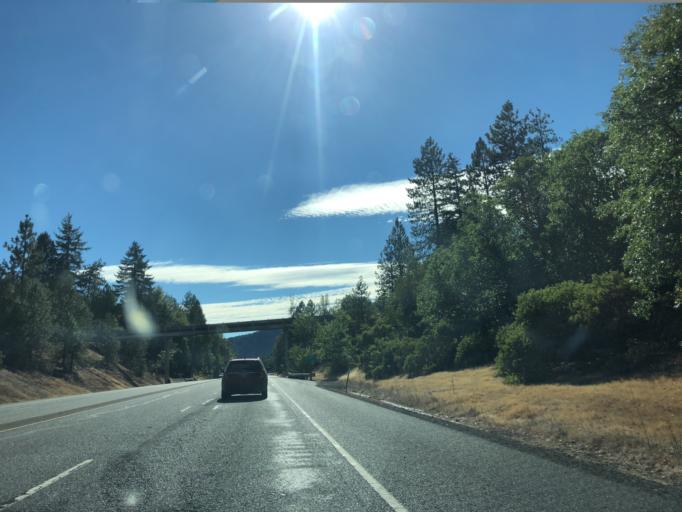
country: US
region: Oregon
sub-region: Josephine County
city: Redwood
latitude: 42.4116
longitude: -123.4199
